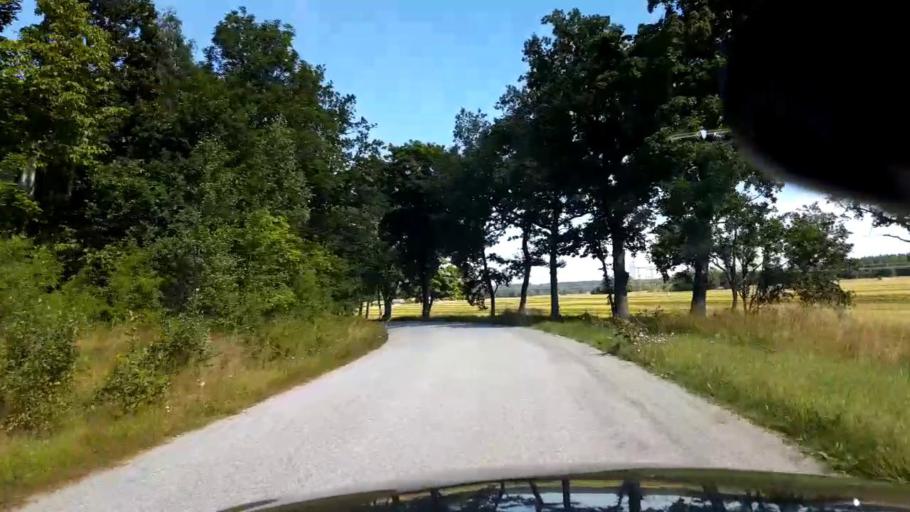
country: SE
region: Stockholm
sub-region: Upplands-Bro Kommun
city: Bro
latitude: 59.5943
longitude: 17.6418
